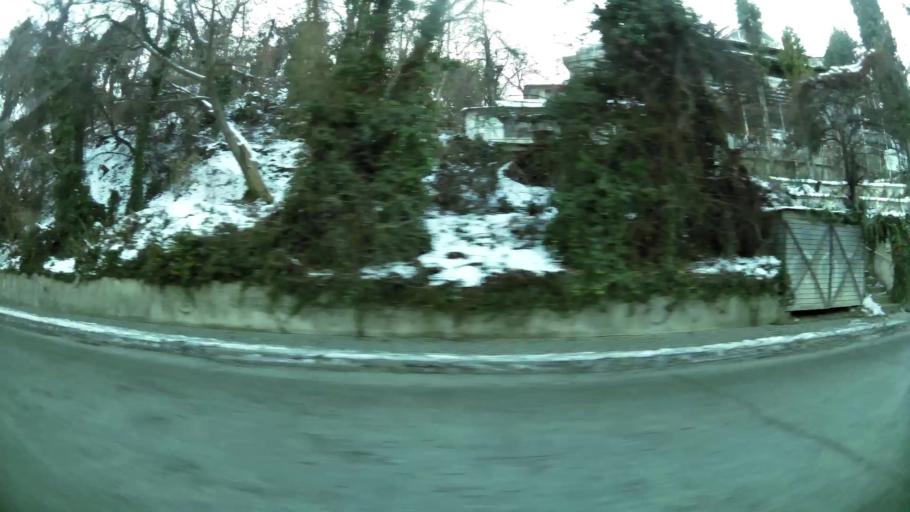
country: MK
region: Karpos
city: Skopje
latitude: 41.9923
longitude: 21.4114
